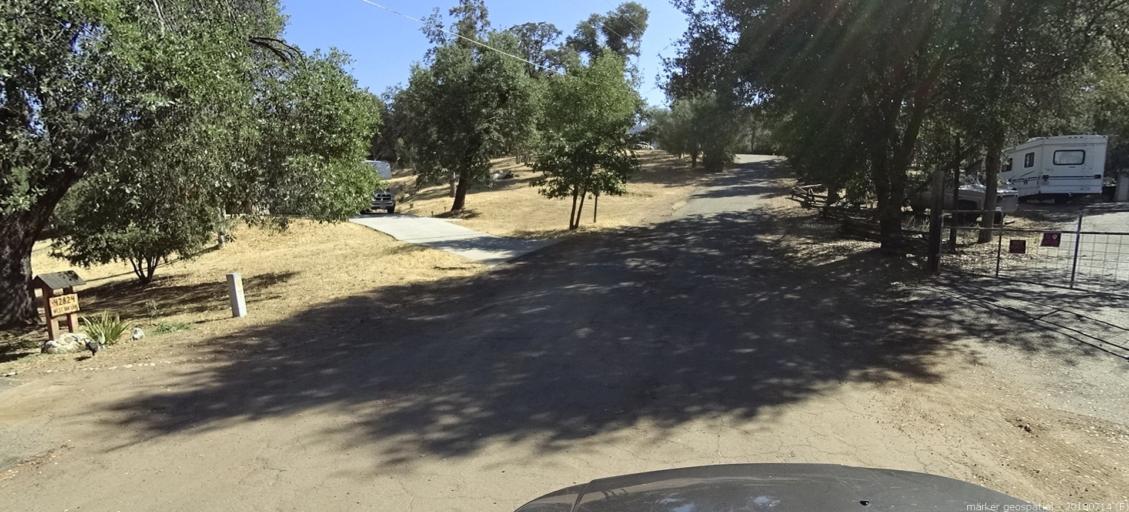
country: US
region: California
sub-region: Madera County
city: Oakhurst
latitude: 37.3720
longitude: -119.6122
